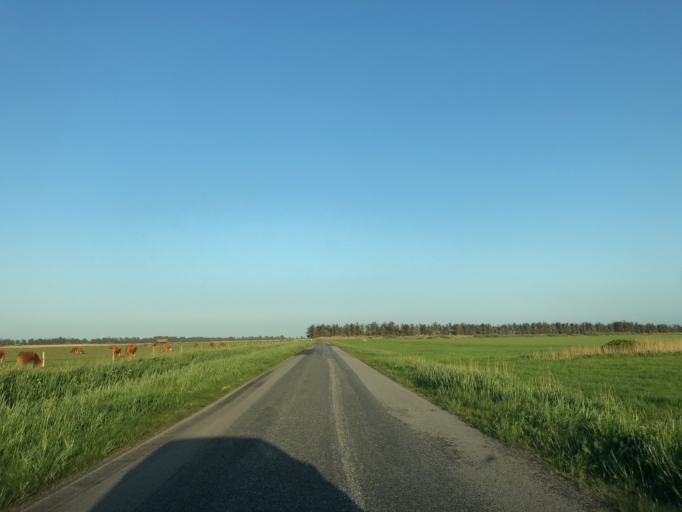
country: DK
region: Central Jutland
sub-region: Ringkobing-Skjern Kommune
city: Ringkobing
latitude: 56.2022
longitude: 8.1480
